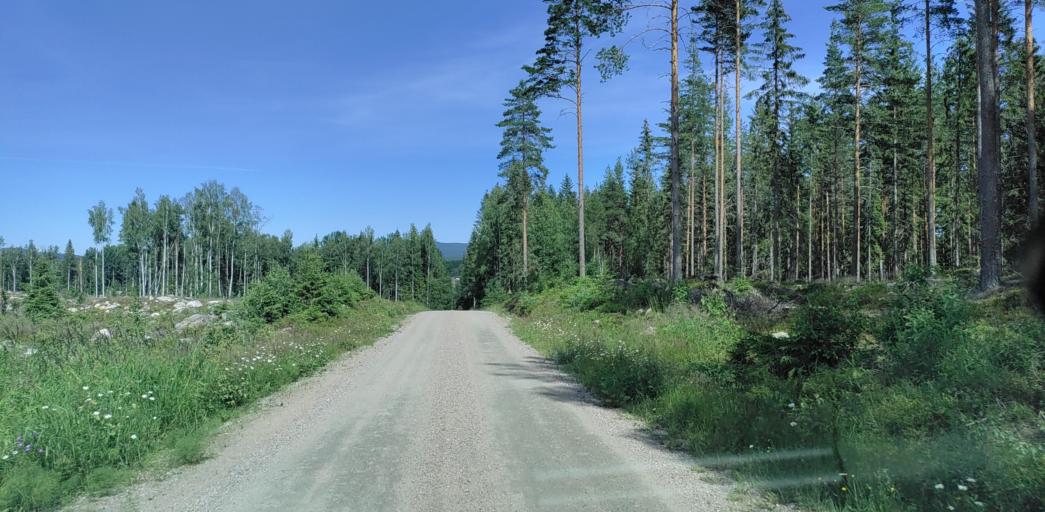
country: SE
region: Vaermland
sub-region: Hagfors Kommun
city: Ekshaerad
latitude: 60.0984
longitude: 13.4389
